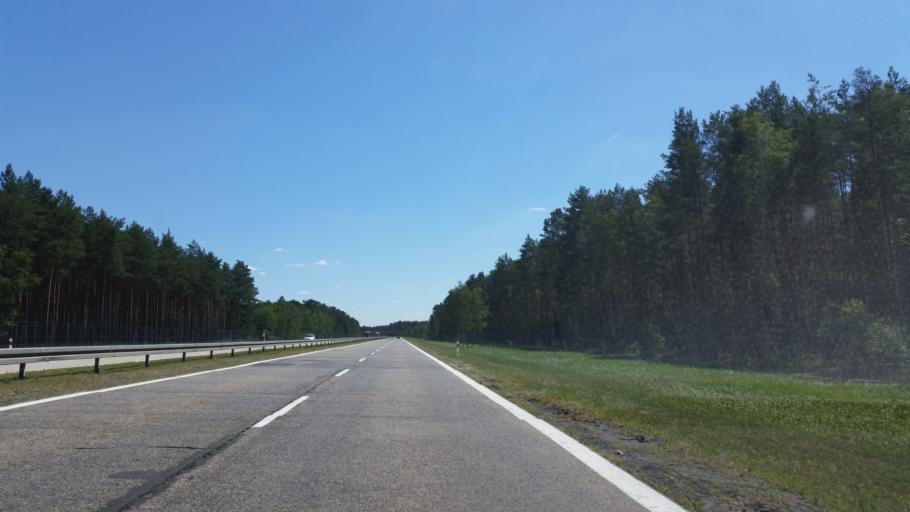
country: PL
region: Lubusz
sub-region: Powiat zaganski
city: Malomice
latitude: 51.4390
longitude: 15.3590
